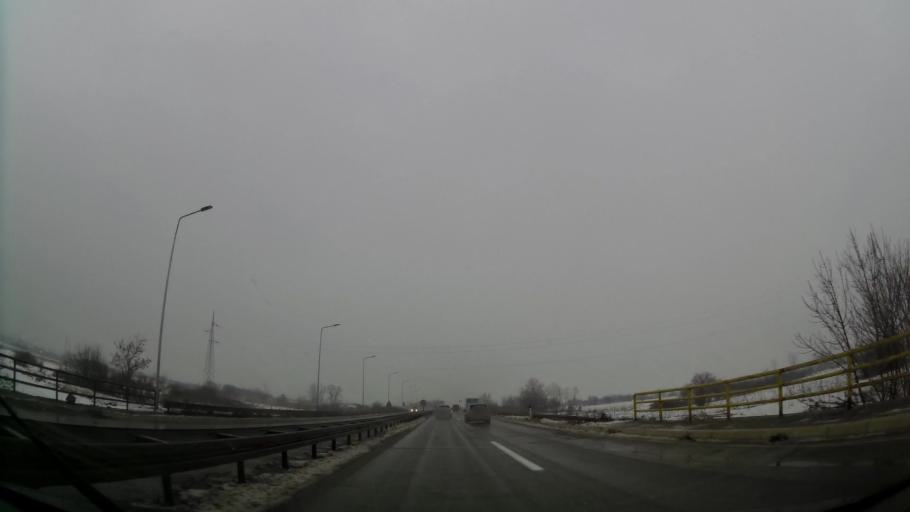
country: RS
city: Ostruznica
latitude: 44.7436
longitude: 20.3633
